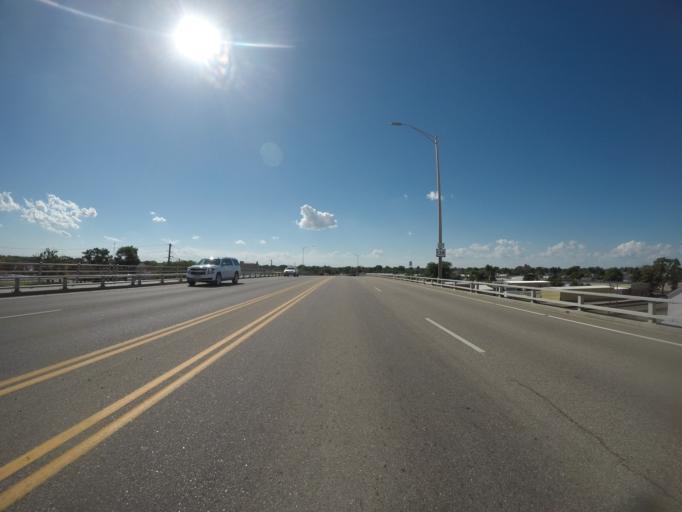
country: US
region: Colorado
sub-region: Logan County
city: Sterling
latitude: 40.6250
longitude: -103.2030
